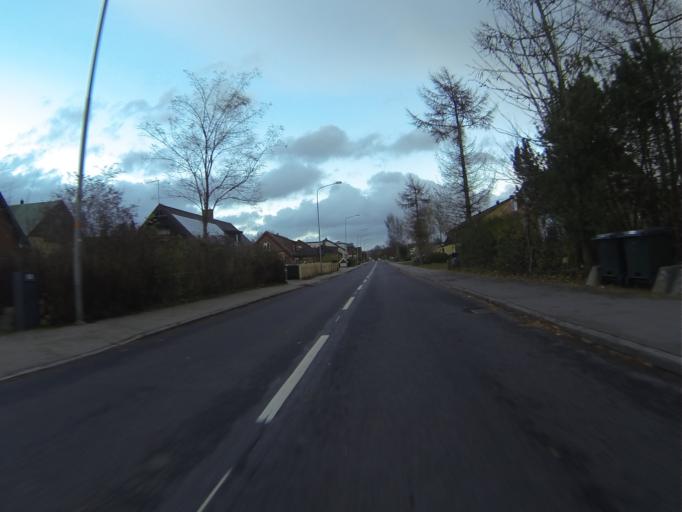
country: SE
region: Skane
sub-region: Lunds Kommun
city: Genarp
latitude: 55.5995
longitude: 13.4013
